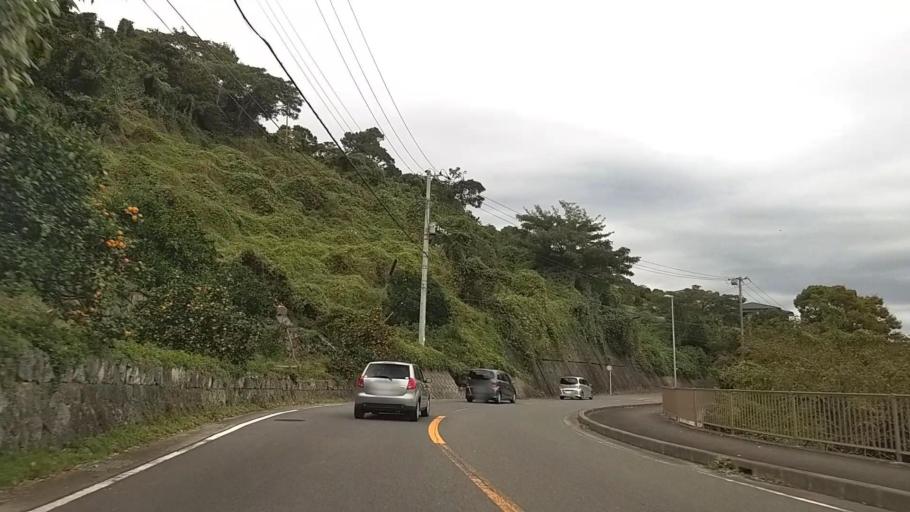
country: JP
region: Kanagawa
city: Yugawara
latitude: 35.1830
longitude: 139.1323
